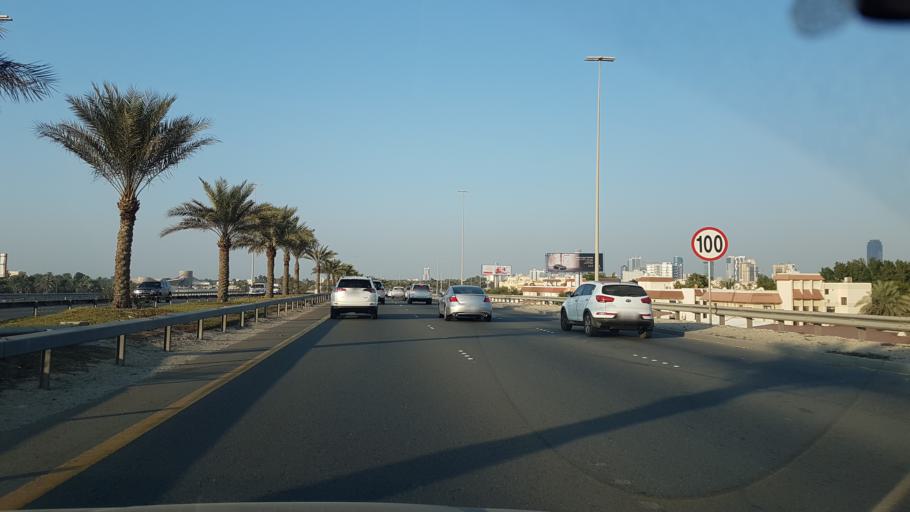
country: BH
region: Manama
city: Jidd Hafs
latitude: 26.2188
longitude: 50.5216
